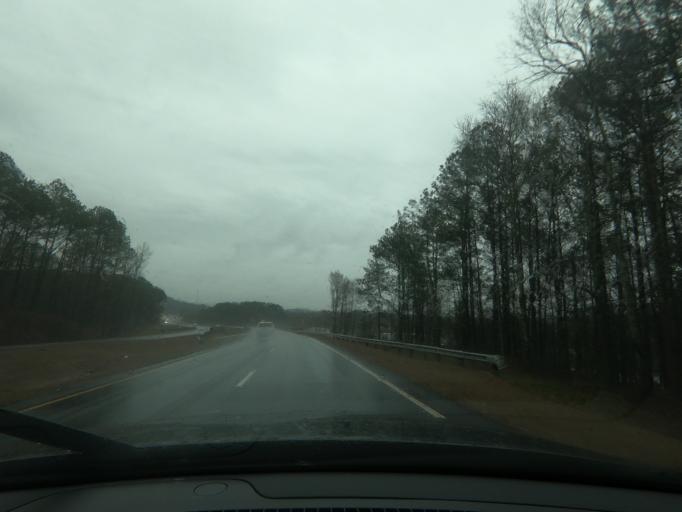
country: US
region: Georgia
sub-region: Bartow County
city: Cartersville
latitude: 34.2215
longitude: -84.8517
